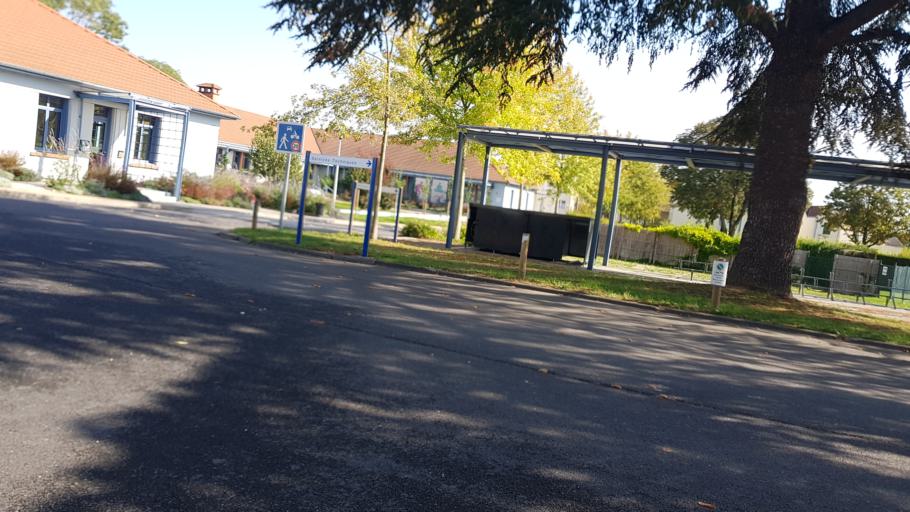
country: FR
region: Poitou-Charentes
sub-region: Departement de la Vienne
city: Chasseneuil-du-Poitou
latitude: 46.6556
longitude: 0.3767
